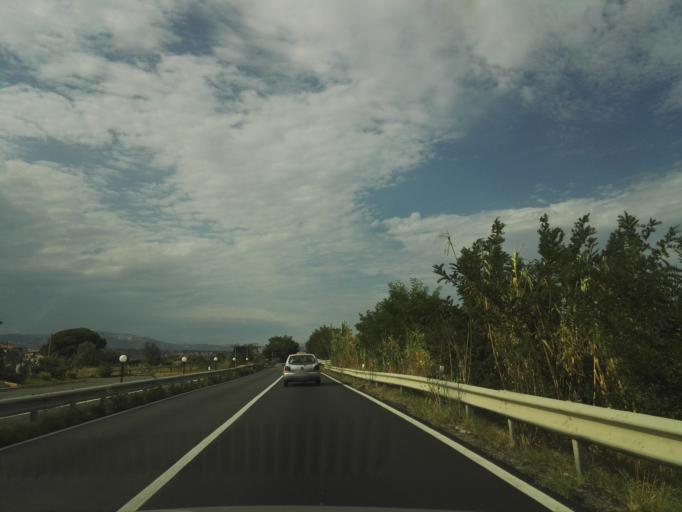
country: IT
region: Calabria
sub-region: Provincia di Catanzaro
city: Marina di Davoli
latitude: 38.6534
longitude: 16.5478
